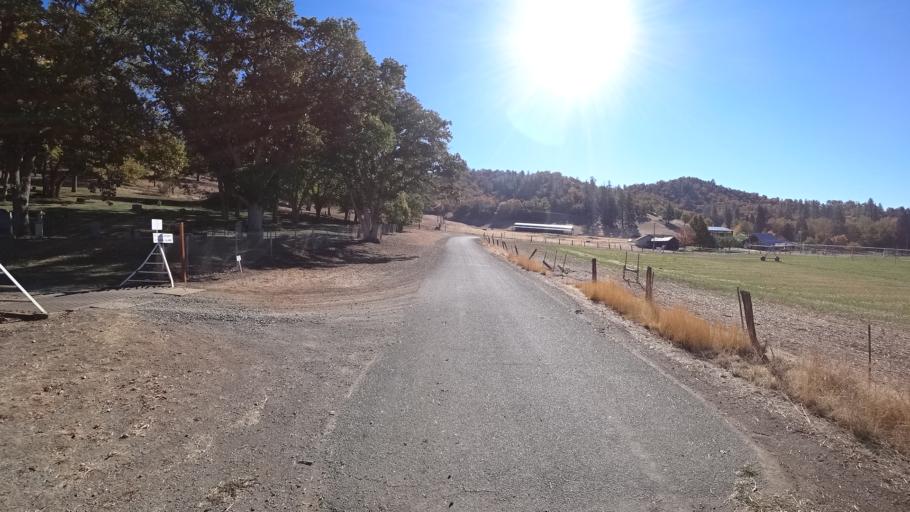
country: US
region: California
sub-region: Siskiyou County
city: Yreka
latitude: 41.5931
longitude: -122.8334
